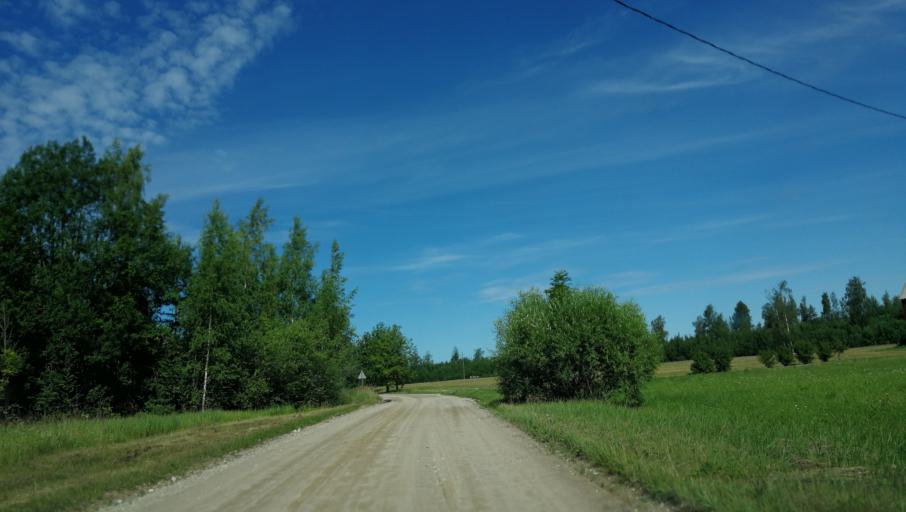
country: LV
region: Gulbenes Rajons
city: Gulbene
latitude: 57.1766
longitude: 26.8737
